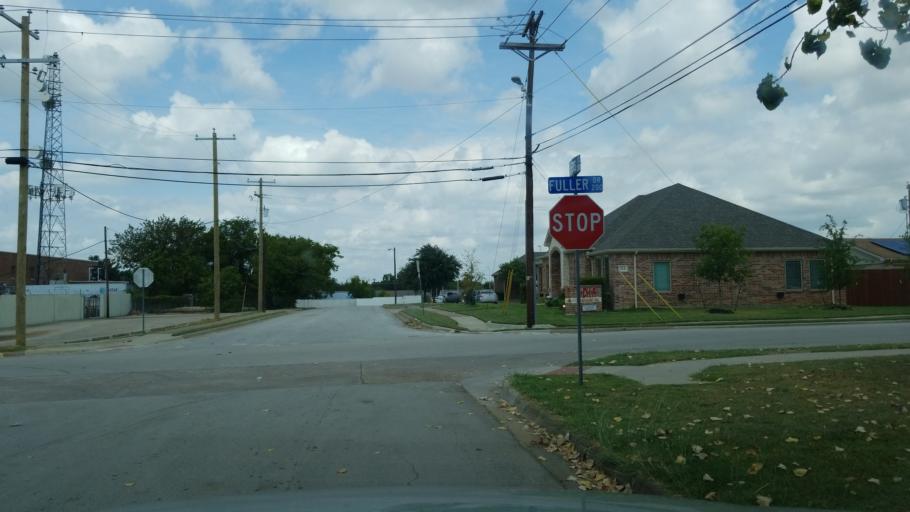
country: US
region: Texas
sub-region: Tarrant County
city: Euless
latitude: 32.8399
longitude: -97.0851
